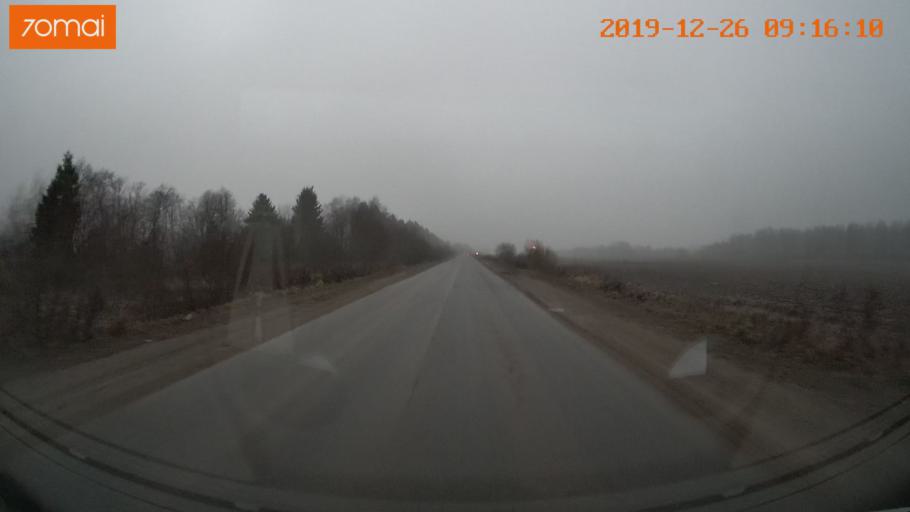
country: RU
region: Vologda
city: Gryazovets
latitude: 58.9127
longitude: 40.2386
